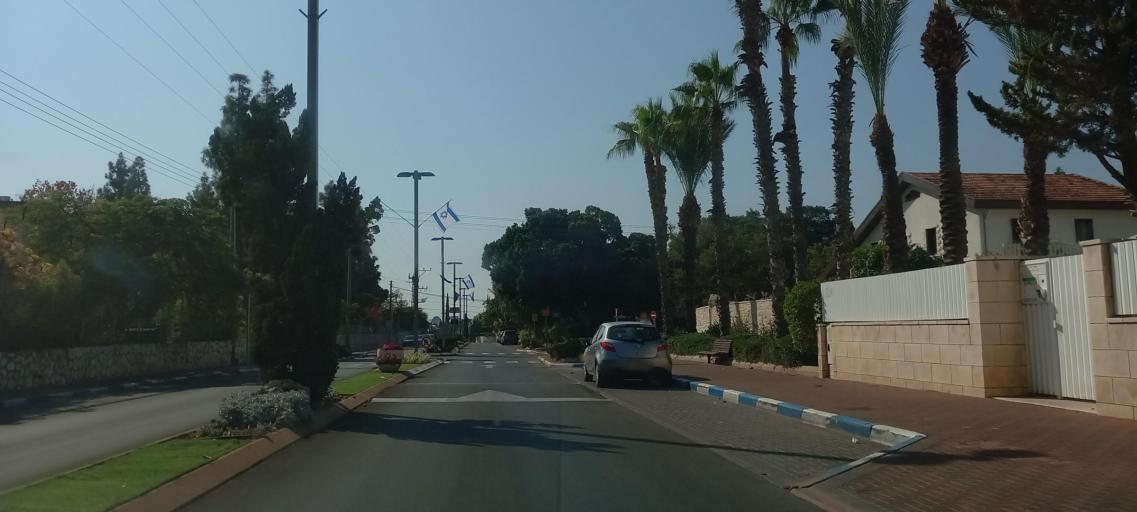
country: IL
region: Tel Aviv
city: Or Yehuda
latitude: 32.0499
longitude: 34.8367
